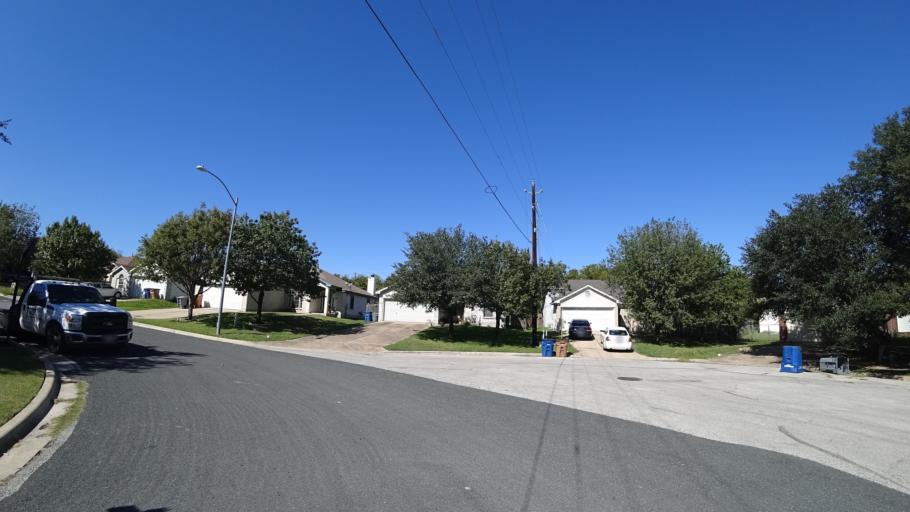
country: US
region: Texas
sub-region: Travis County
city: Hornsby Bend
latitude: 30.3063
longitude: -97.6393
